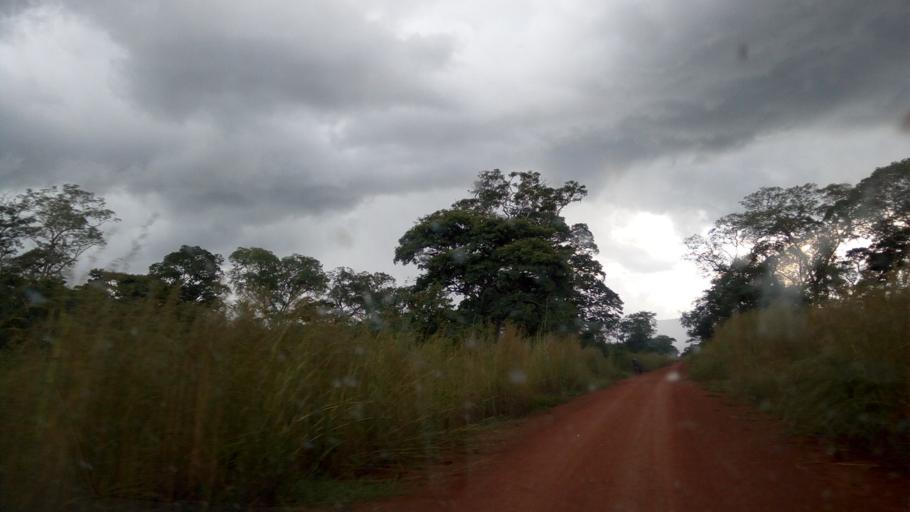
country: ZM
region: Northern
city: Kaputa
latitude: -8.0695
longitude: 29.1704
